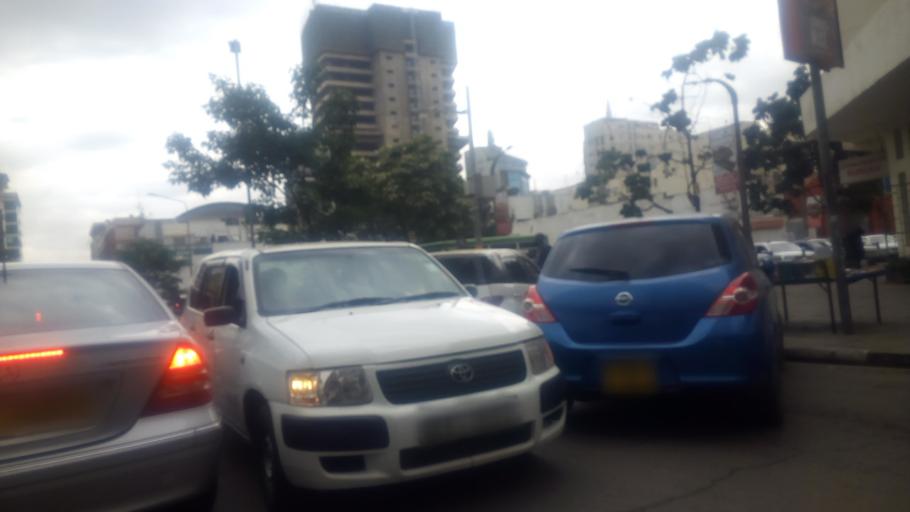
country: KE
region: Nairobi Area
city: Nairobi
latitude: -1.2818
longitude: 36.8165
